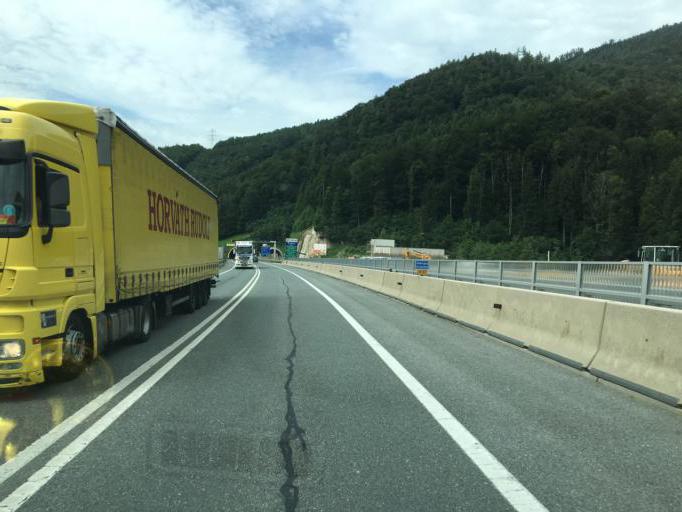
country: AT
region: Upper Austria
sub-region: Politischer Bezirk Kirchdorf an der Krems
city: Micheldorf in Oberoesterreich
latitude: 47.8173
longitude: 14.1696
